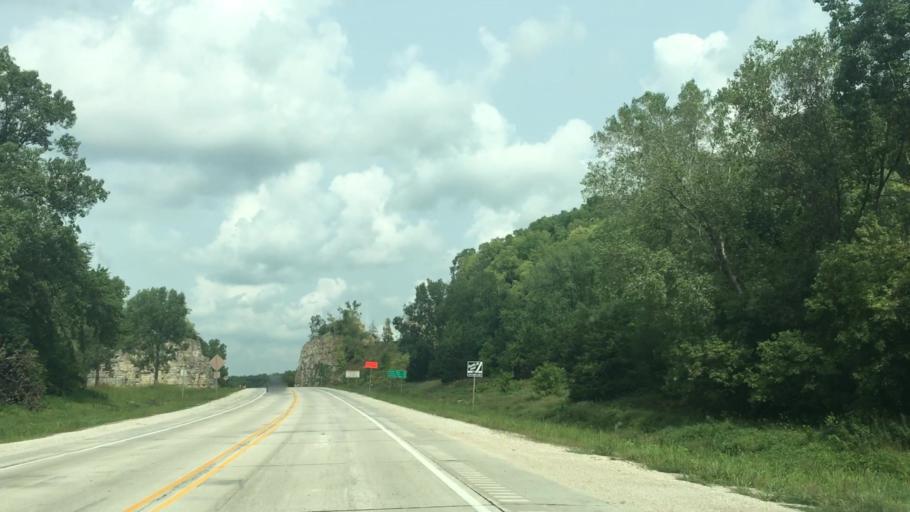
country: US
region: Iowa
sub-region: Winneshiek County
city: Decorah
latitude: 43.2933
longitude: -91.8064
